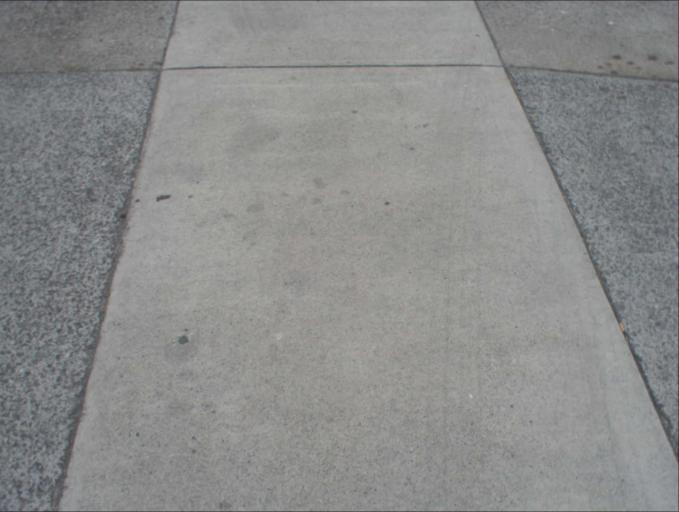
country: AU
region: Queensland
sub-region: Logan
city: Beenleigh
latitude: -27.7145
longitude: 153.1930
